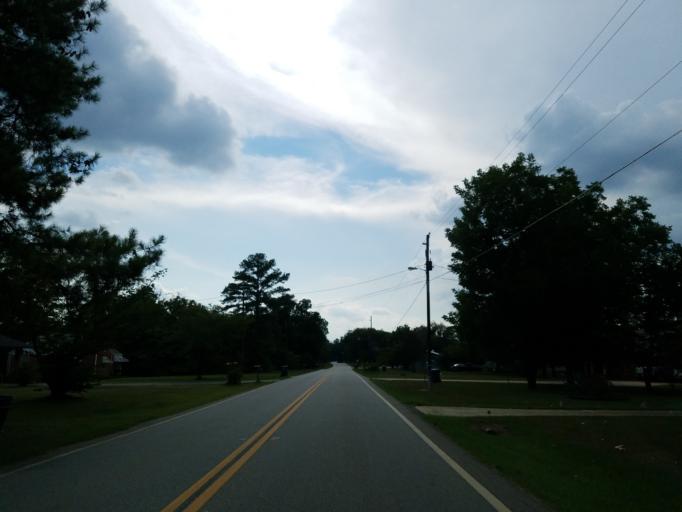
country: US
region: Georgia
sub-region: Dooly County
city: Unadilla
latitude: 32.2604
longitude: -83.7256
